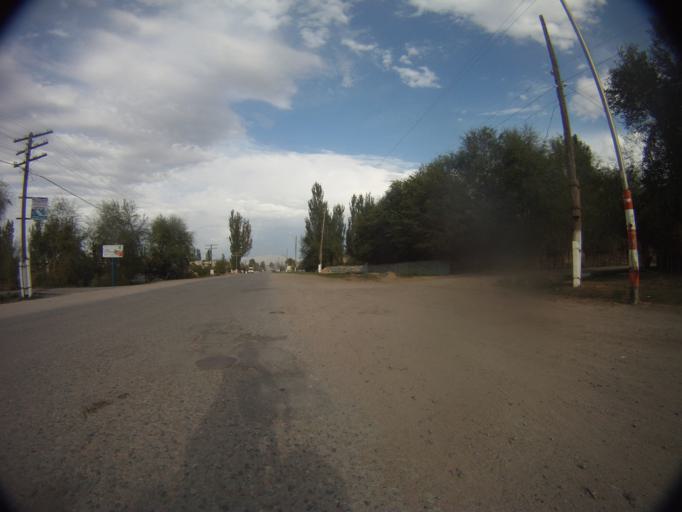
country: KG
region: Ysyk-Koel
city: Pokrovka
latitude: 42.3209
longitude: 77.9124
